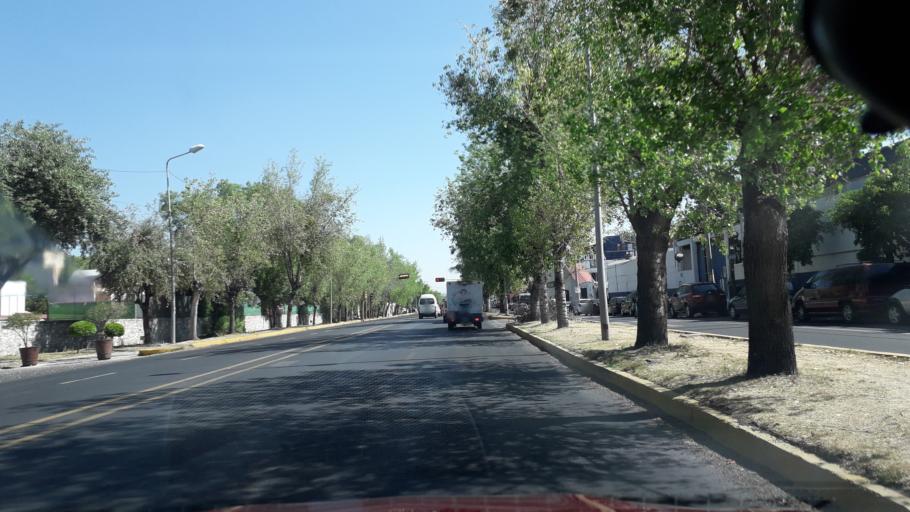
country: MX
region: Puebla
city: Puebla
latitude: 19.0750
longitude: -98.2180
